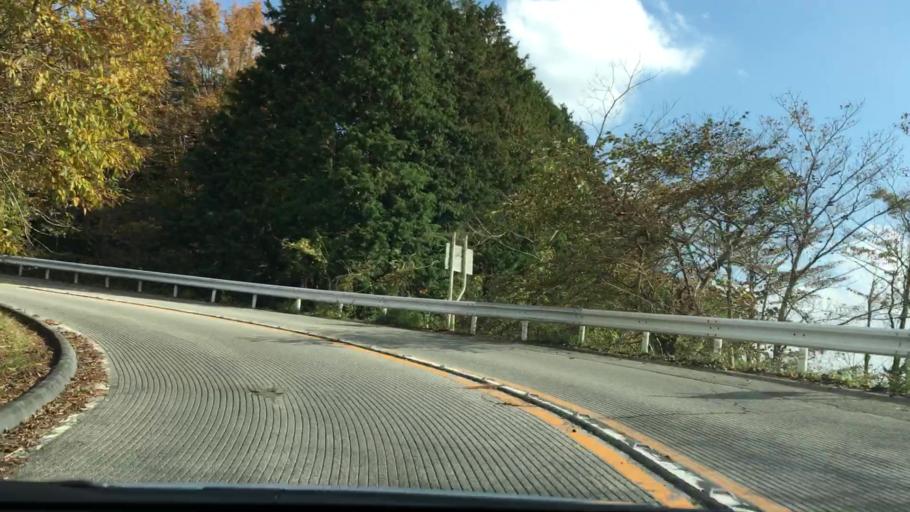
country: JP
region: Shizuoka
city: Gotemba
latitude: 35.3863
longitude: 138.9456
